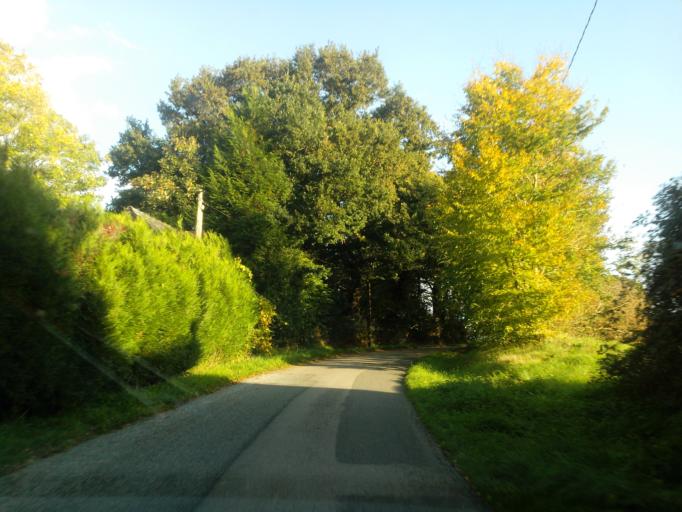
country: FR
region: Brittany
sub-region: Departement du Morbihan
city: Guilliers
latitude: 48.1097
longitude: -2.3635
